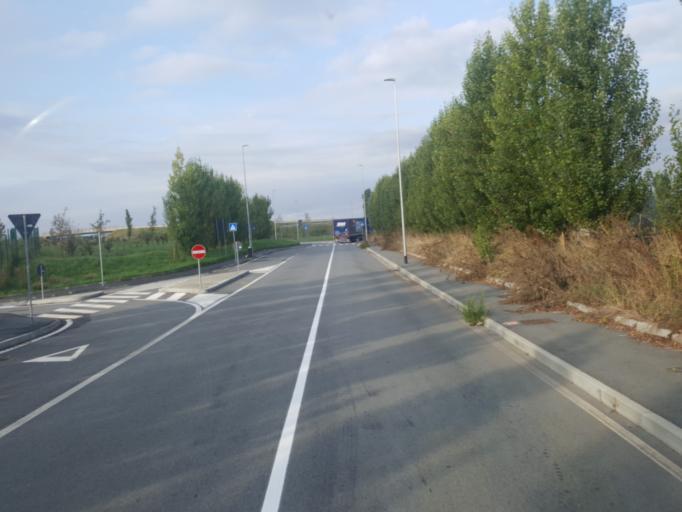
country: IT
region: Piedmont
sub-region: Provincia di Vercelli
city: Asigliano Vercellese
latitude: 45.2924
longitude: 8.3927
